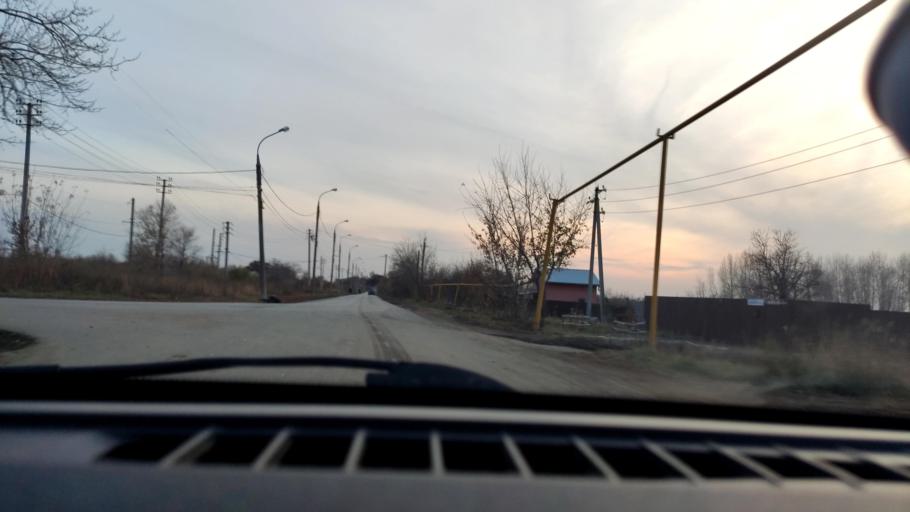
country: RU
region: Samara
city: Samara
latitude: 53.1476
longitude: 50.1354
